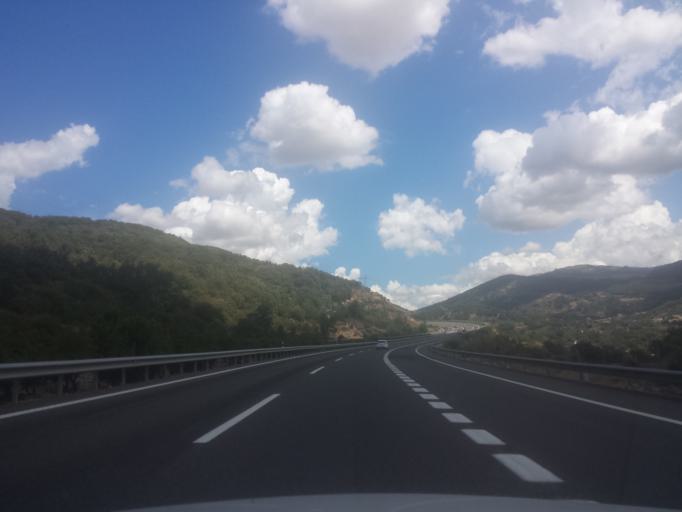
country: ES
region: Extremadura
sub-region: Provincia de Caceres
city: Banos de Montemayor
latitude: 40.3013
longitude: -5.8868
